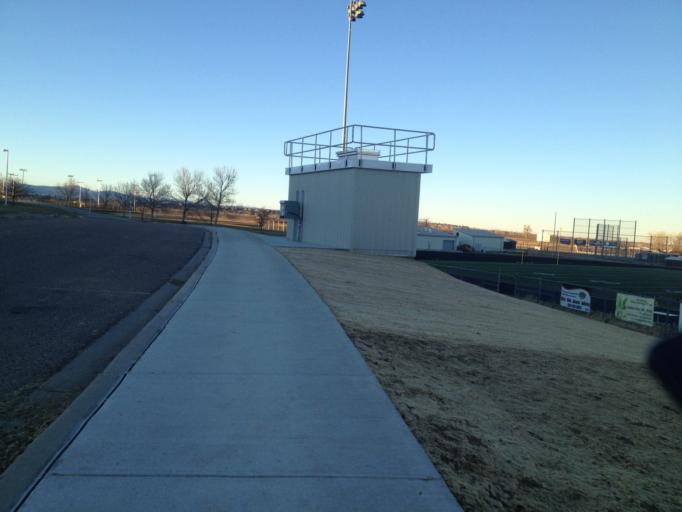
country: US
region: Colorado
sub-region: Boulder County
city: Louisville
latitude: 39.9520
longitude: -105.1394
